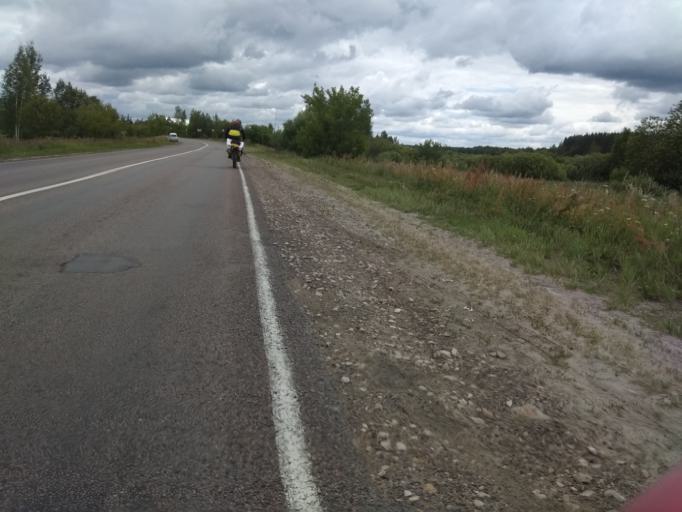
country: RU
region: Moskovskaya
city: Kerva
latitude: 55.5857
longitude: 39.6991
